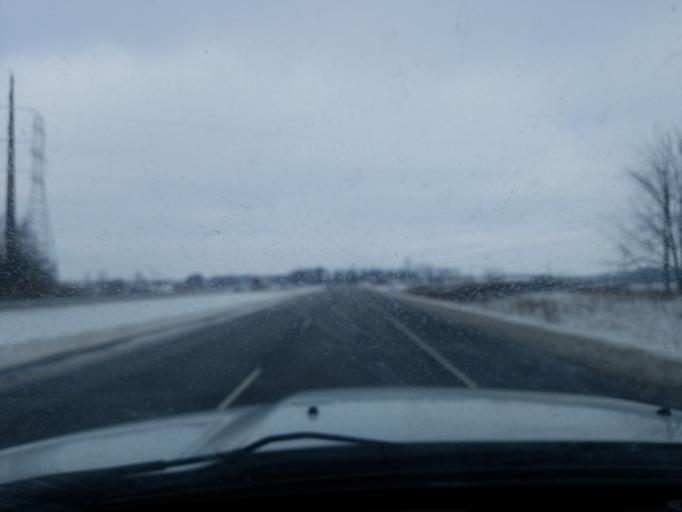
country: US
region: Indiana
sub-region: Marshall County
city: Plymouth
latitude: 41.2850
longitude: -86.2708
